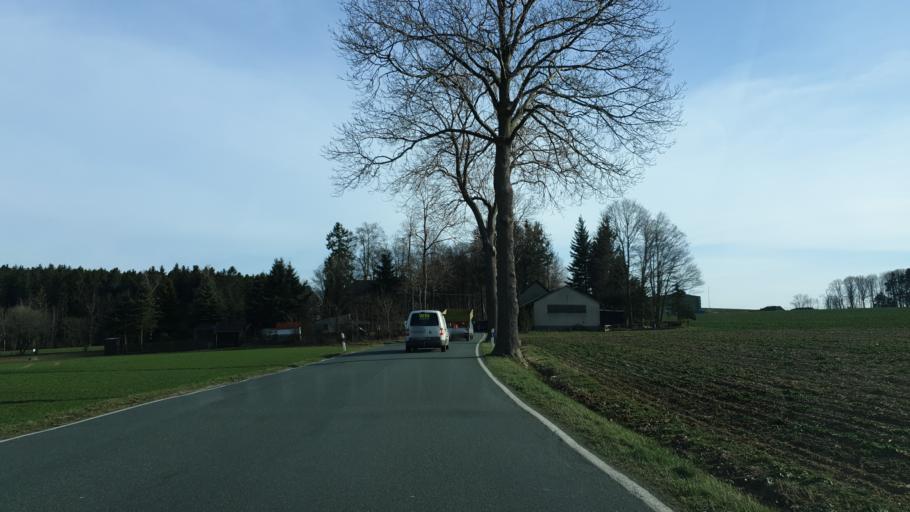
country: DE
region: Saxony
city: Zwonitz
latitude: 50.6483
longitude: 12.7803
